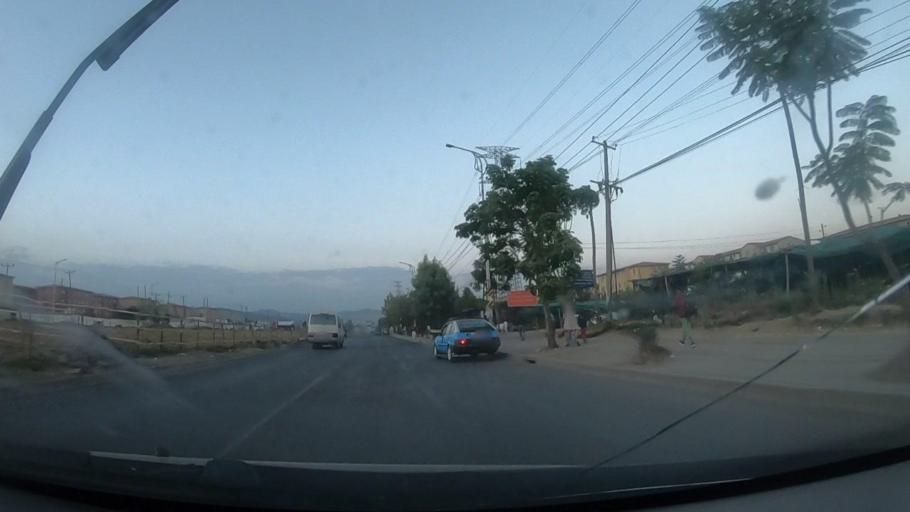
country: ET
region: Adis Abeba
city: Addis Ababa
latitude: 9.0473
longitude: 38.8783
